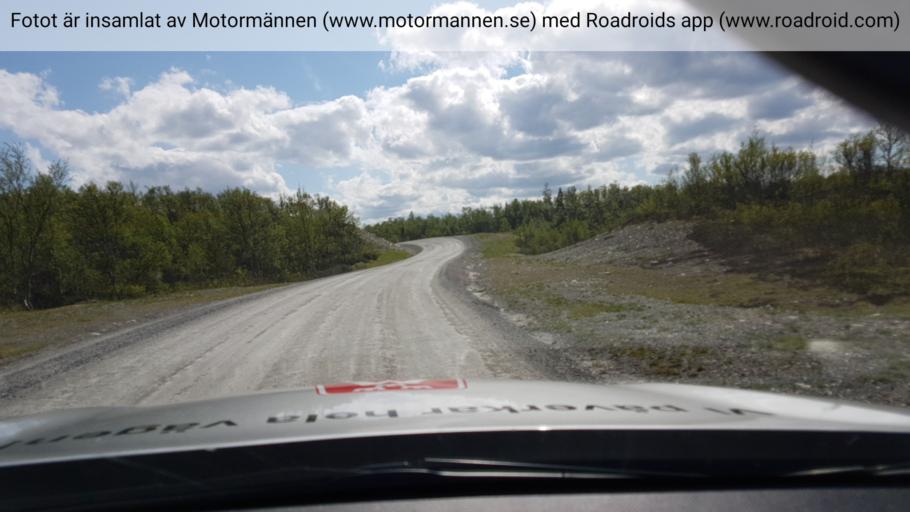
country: SE
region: Jaemtland
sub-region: Are Kommun
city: Are
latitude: 62.6427
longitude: 12.6579
